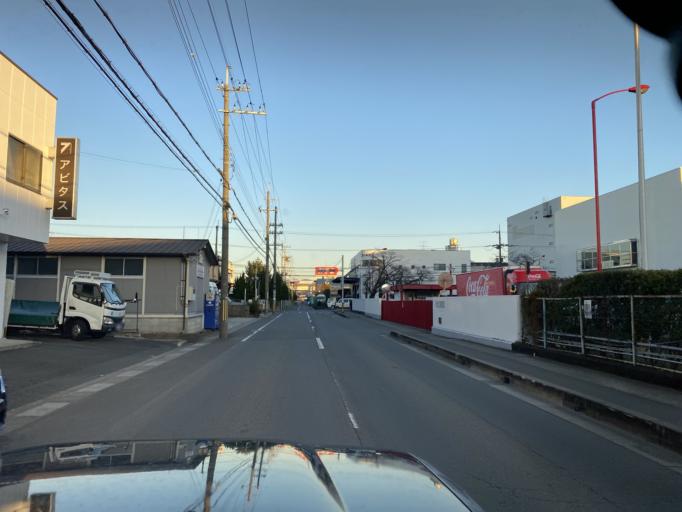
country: JP
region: Kyoto
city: Yawata
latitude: 34.8845
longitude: 135.7445
